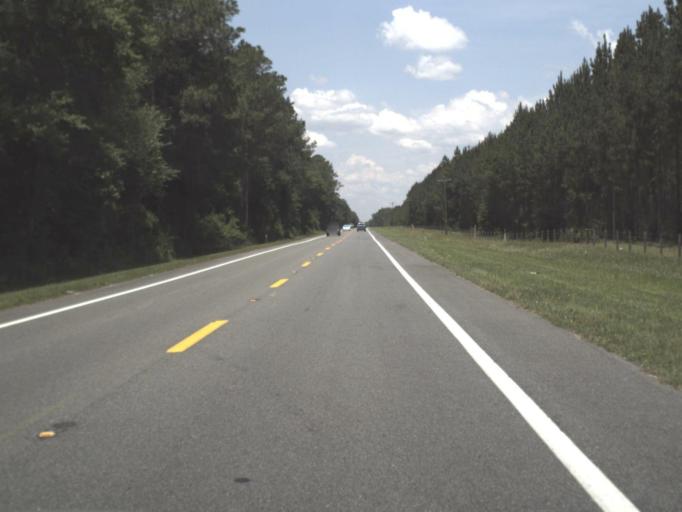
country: US
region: Florida
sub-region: Union County
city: Lake Butler
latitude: 30.0458
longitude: -82.3944
